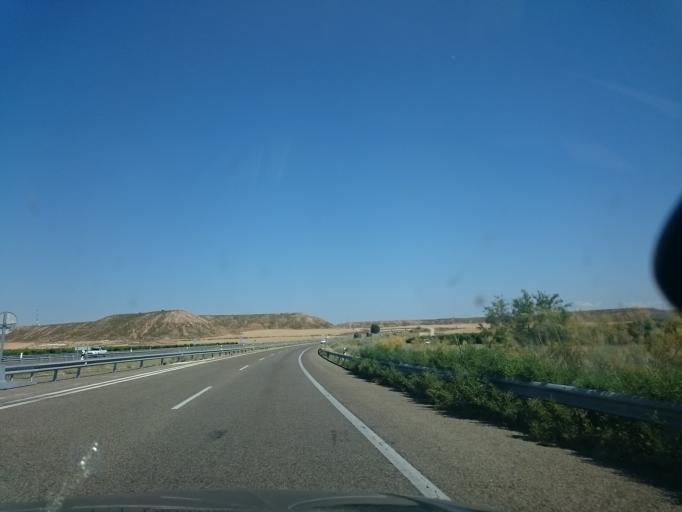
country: ES
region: Aragon
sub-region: Provincia de Huesca
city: Candasnos
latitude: 41.4958
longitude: 0.1411
